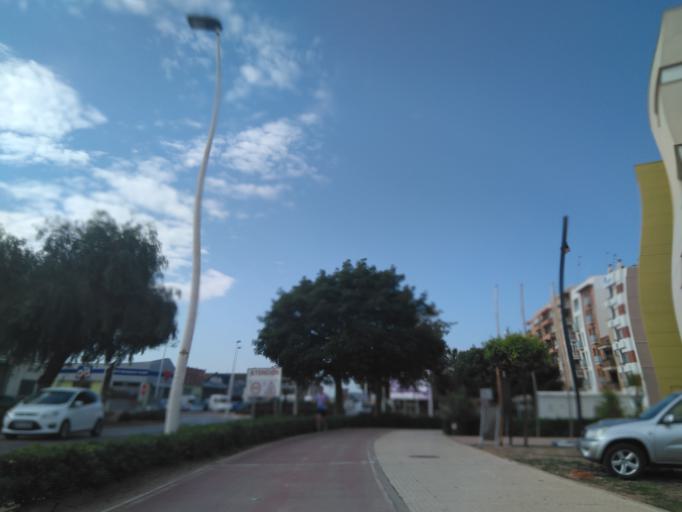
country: ES
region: Valencia
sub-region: Provincia de Valencia
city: Alboraya
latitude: 39.5017
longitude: -0.3461
